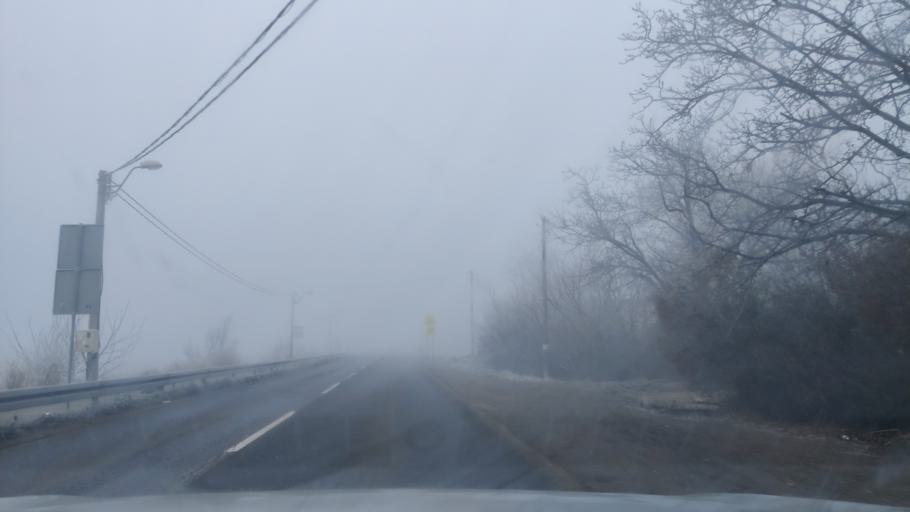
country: RS
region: Central Serbia
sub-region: Belgrade
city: Stari Grad
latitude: 44.8902
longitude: 20.4590
